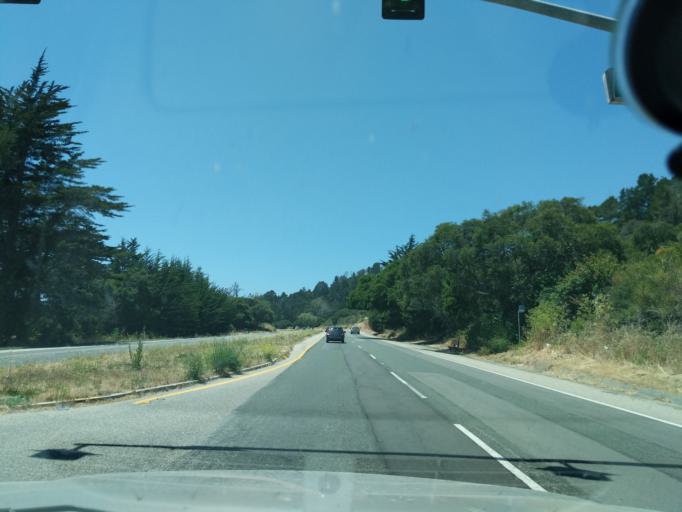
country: US
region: California
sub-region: Monterey County
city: Carmel-by-the-Sea
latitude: 36.5418
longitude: -121.8801
